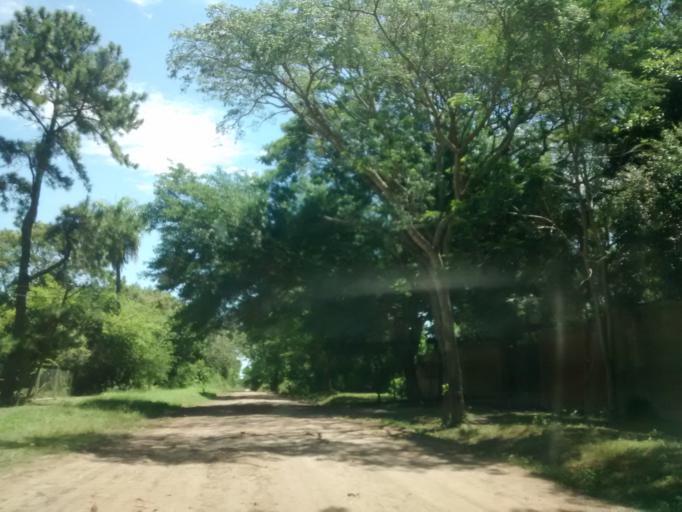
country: AR
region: Chaco
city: Resistencia
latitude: -27.4200
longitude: -58.9668
